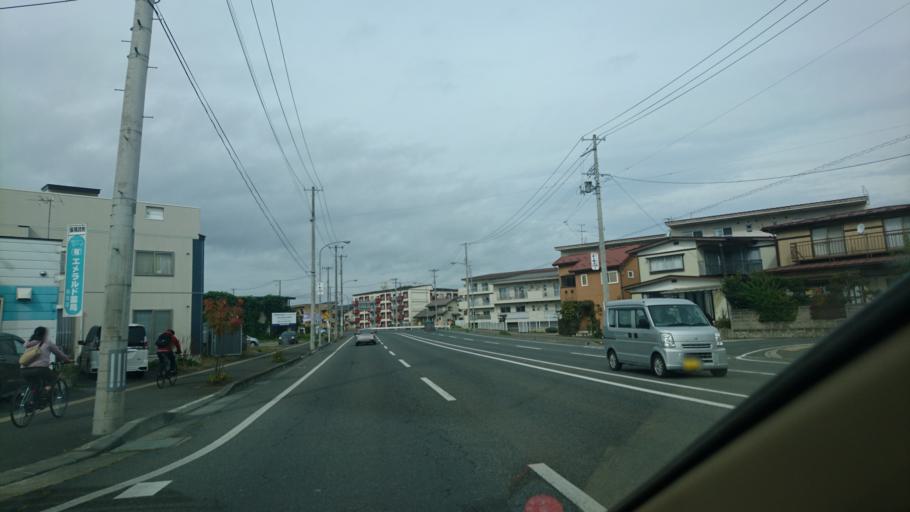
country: JP
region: Iwate
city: Morioka-shi
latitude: 39.6838
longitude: 141.1558
